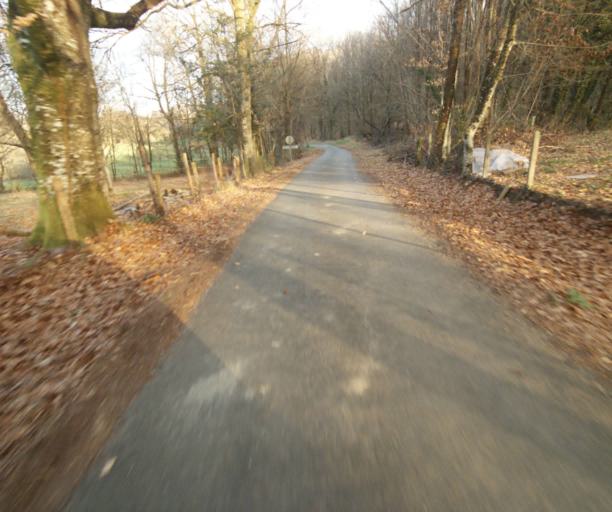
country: FR
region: Limousin
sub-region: Departement de la Correze
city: Uzerche
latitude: 45.3688
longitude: 1.5757
